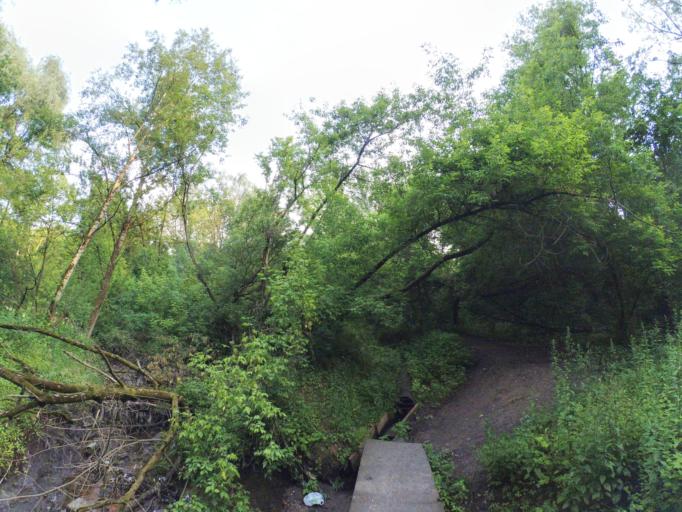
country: RU
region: Moscow
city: Shchukino
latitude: 55.7968
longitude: 37.4488
